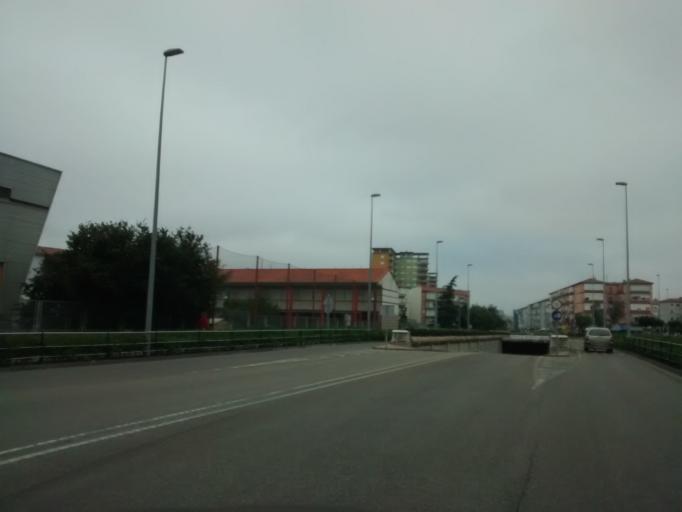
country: ES
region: Cantabria
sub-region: Provincia de Cantabria
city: Torrelavega
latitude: 43.3429
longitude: -4.0623
